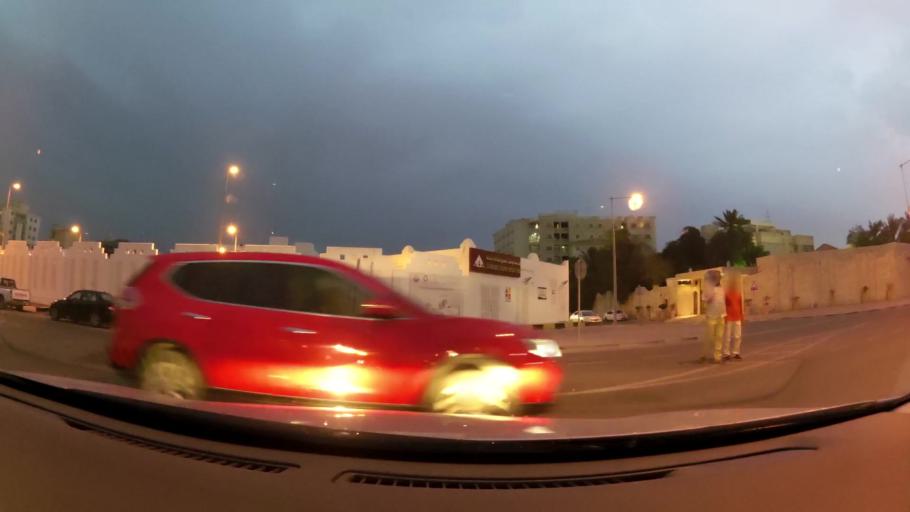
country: QA
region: Baladiyat ad Dawhah
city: Doha
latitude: 25.2657
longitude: 51.5196
